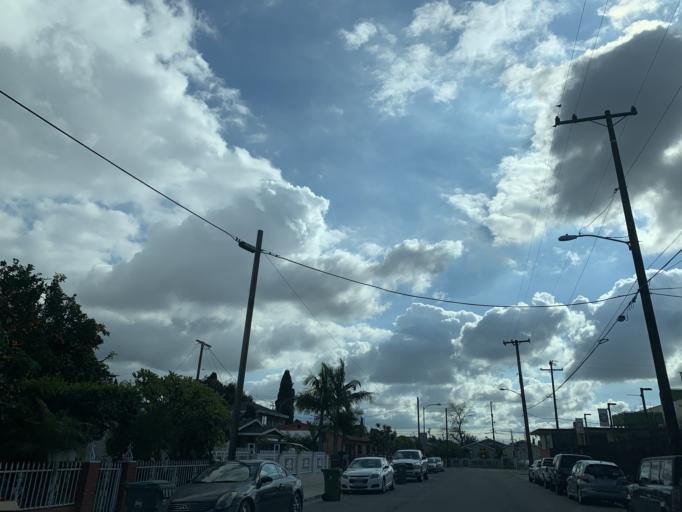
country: US
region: California
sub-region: Los Angeles County
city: Florence-Graham
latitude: 33.9634
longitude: -118.2421
